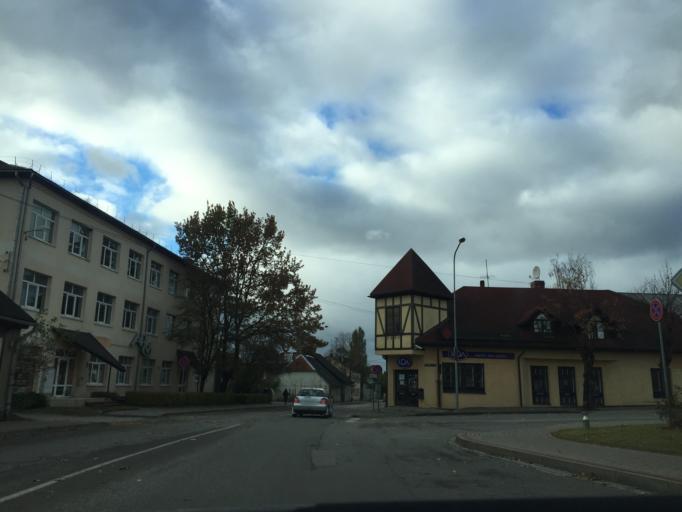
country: LV
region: Tukuma Rajons
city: Tukums
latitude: 56.9668
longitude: 23.1525
